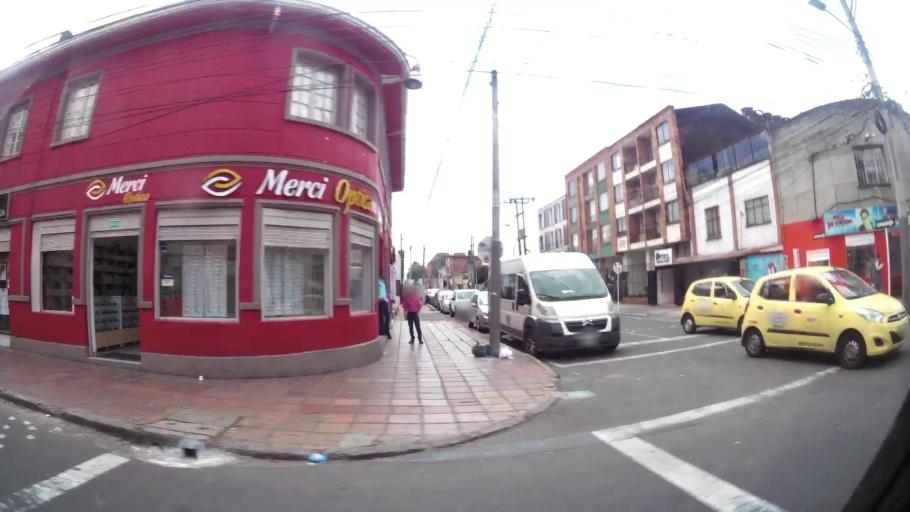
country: CO
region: Bogota D.C.
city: Bogota
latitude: 4.6378
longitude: -74.0689
